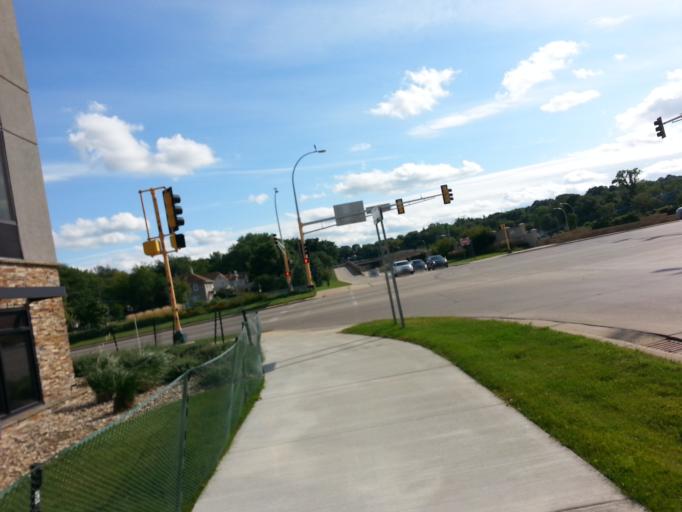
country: US
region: Minnesota
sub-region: Olmsted County
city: Rochester
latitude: 44.0220
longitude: -92.4875
